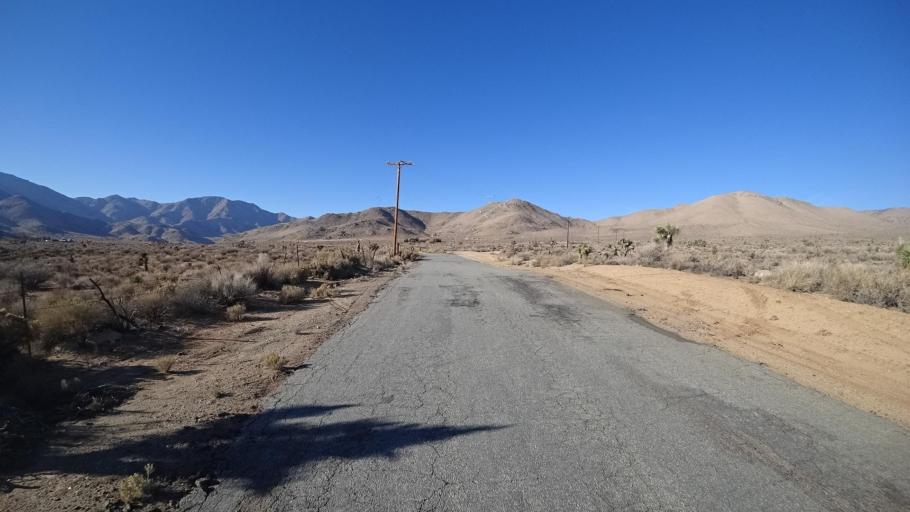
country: US
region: California
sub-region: Kern County
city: Weldon
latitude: 35.5555
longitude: -118.2150
